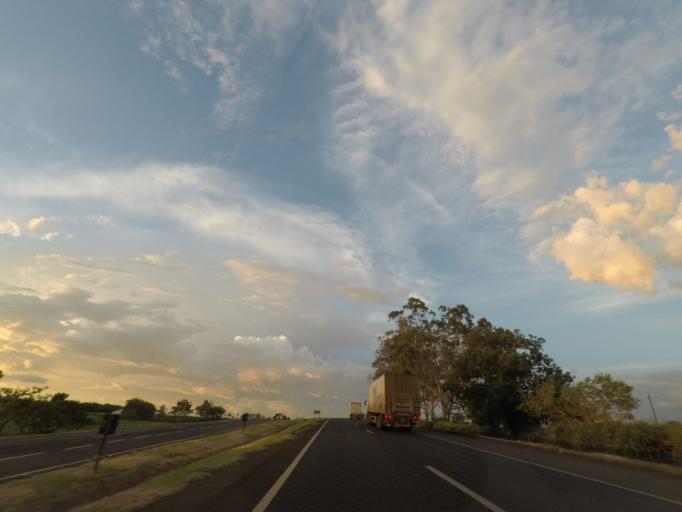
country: BR
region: Minas Gerais
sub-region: Uberaba
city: Uberaba
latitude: -19.6727
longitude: -47.9974
